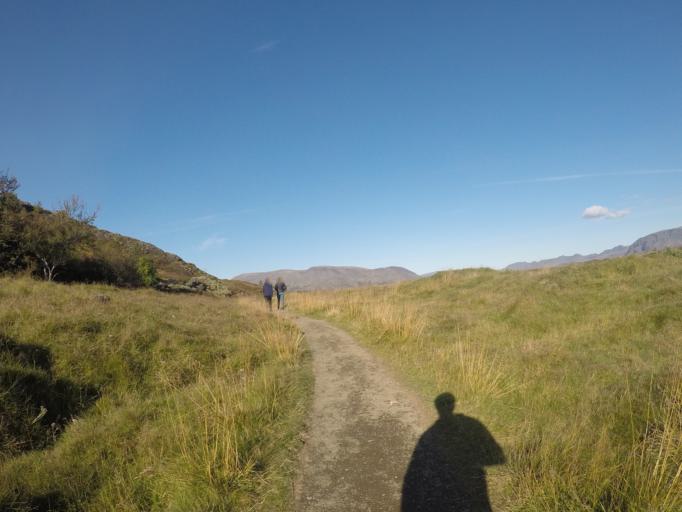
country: IS
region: South
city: Hveragerdi
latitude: 64.2575
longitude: -21.1238
